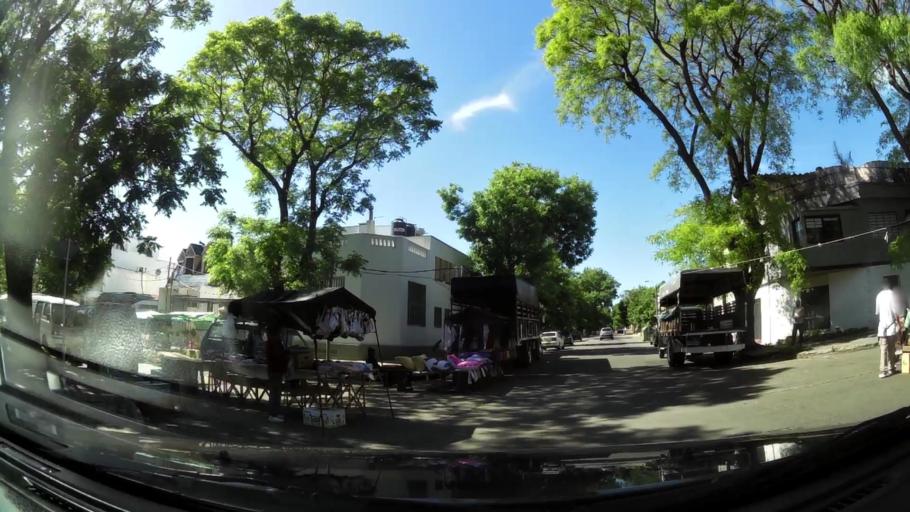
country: UY
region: Montevideo
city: Montevideo
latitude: -34.9007
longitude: -56.1512
